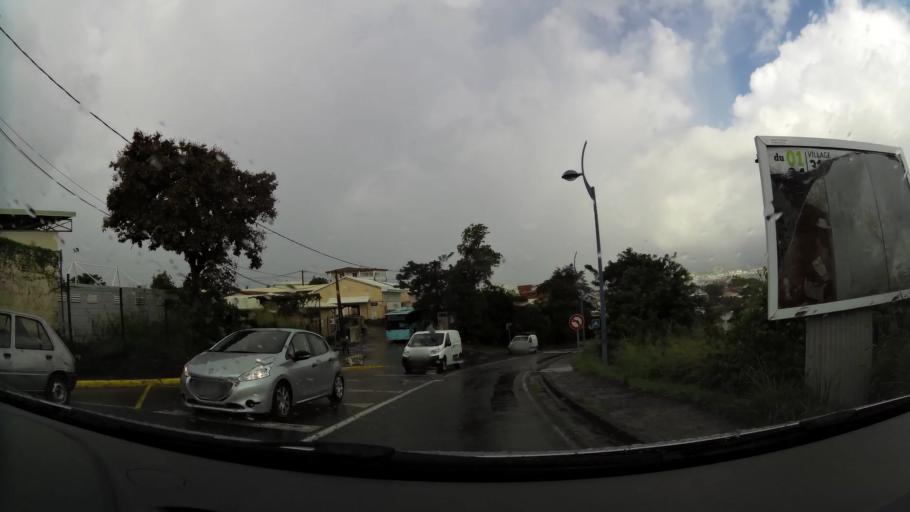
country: MQ
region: Martinique
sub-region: Martinique
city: Les Trois-Ilets
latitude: 14.5494
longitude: -61.0504
